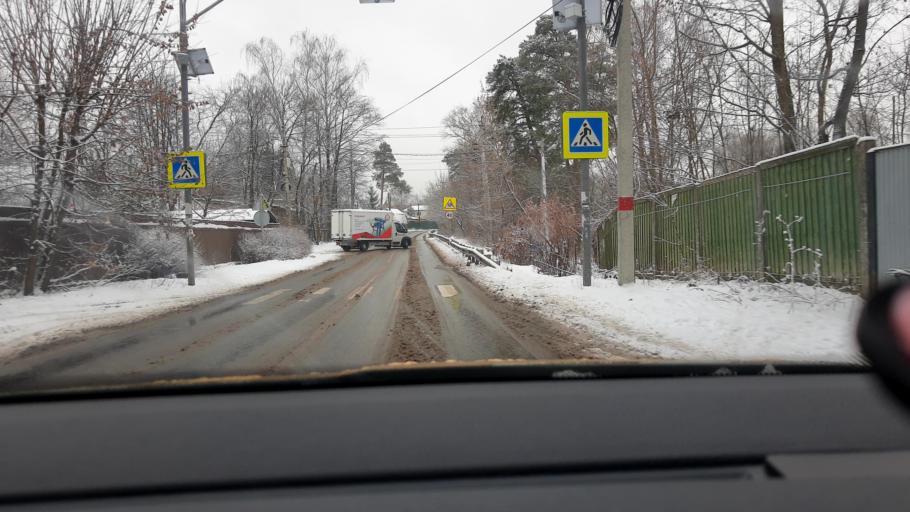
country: RU
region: Moskovskaya
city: Mamontovka
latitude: 55.9724
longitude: 37.8245
